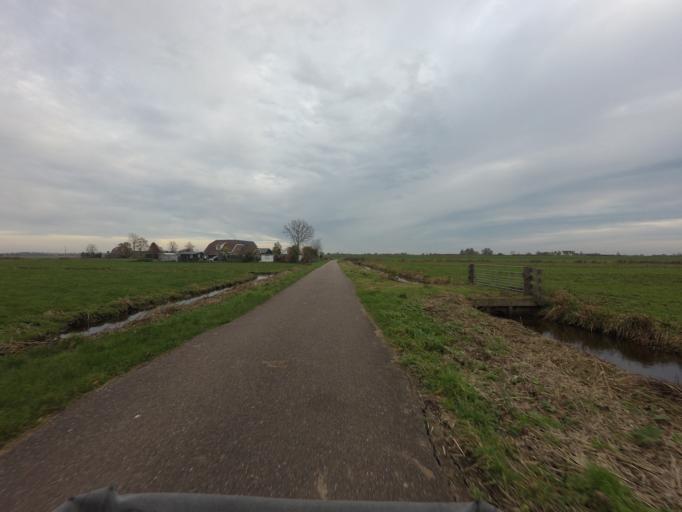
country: NL
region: North Holland
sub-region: Gemeente Ouder-Amstel
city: Ouderkerk aan de Amstel
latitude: 52.2840
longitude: 4.9293
